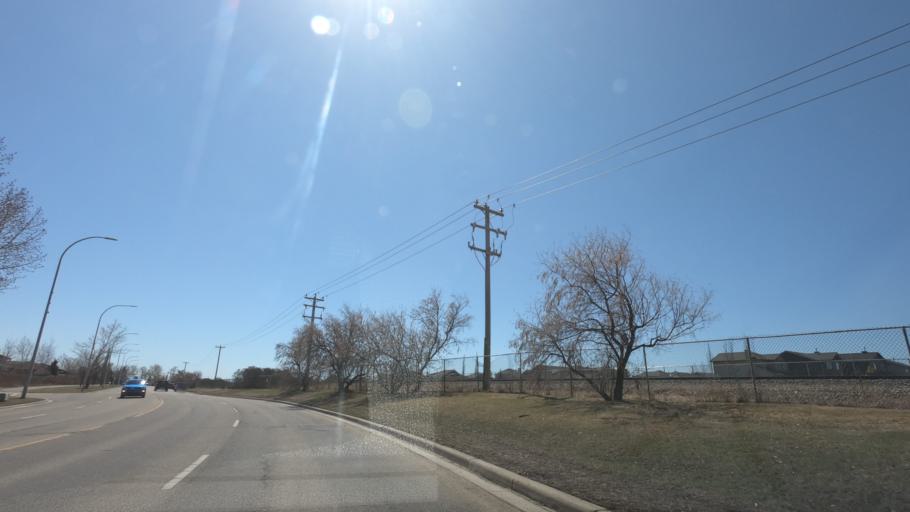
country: CA
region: Alberta
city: Airdrie
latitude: 51.2766
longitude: -114.0140
